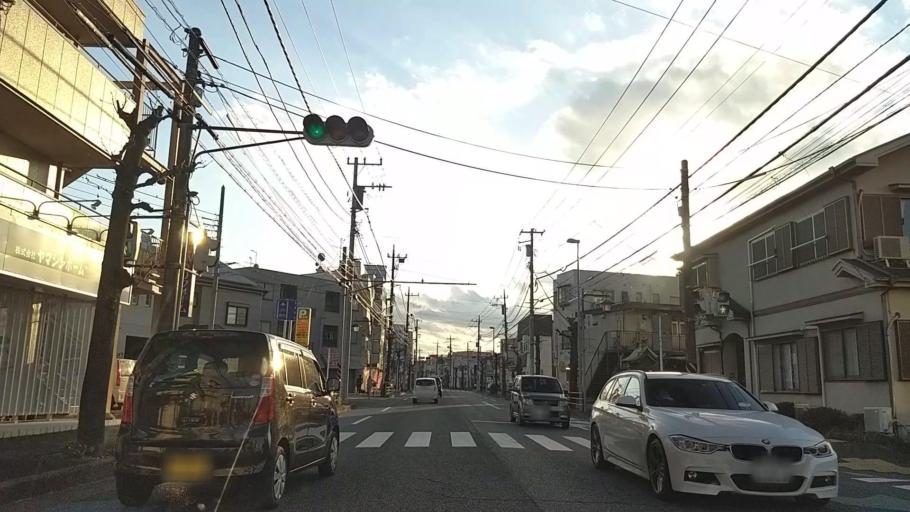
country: JP
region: Kanagawa
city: Atsugi
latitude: 35.4348
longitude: 139.3679
